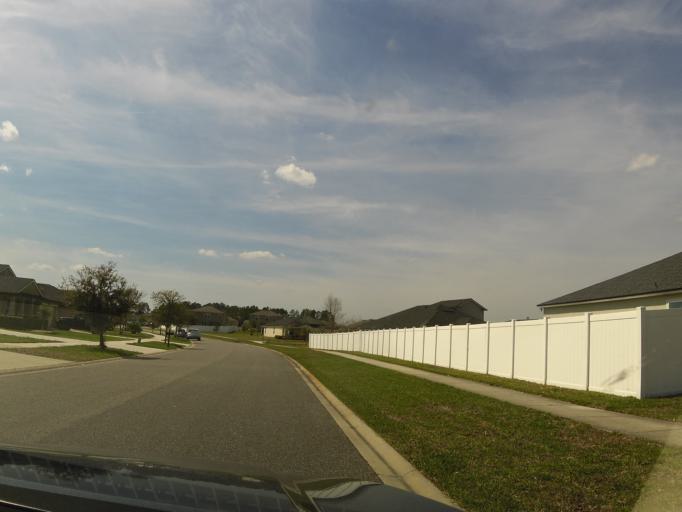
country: US
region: Florida
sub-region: Clay County
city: Middleburg
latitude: 30.0972
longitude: -81.8595
